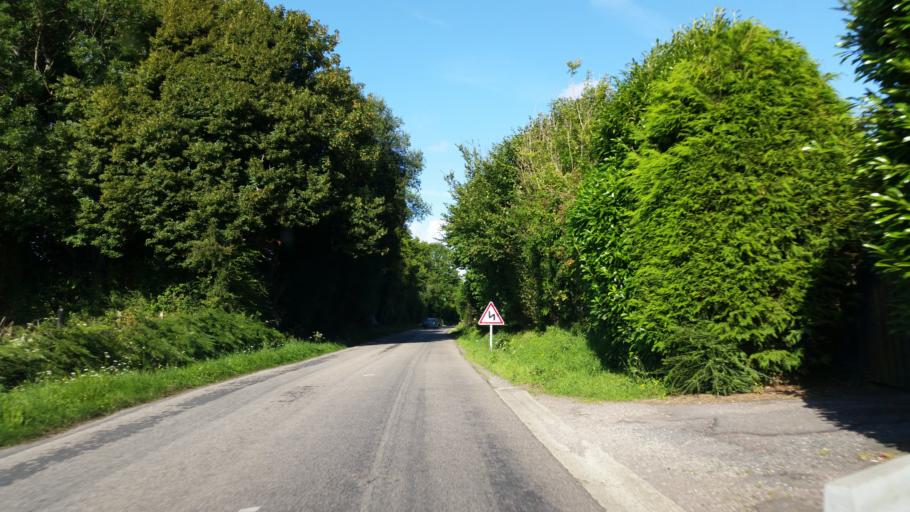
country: FR
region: Lower Normandy
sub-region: Departement du Calvados
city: Saint-Gatien-des-Bois
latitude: 49.3587
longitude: 0.1805
